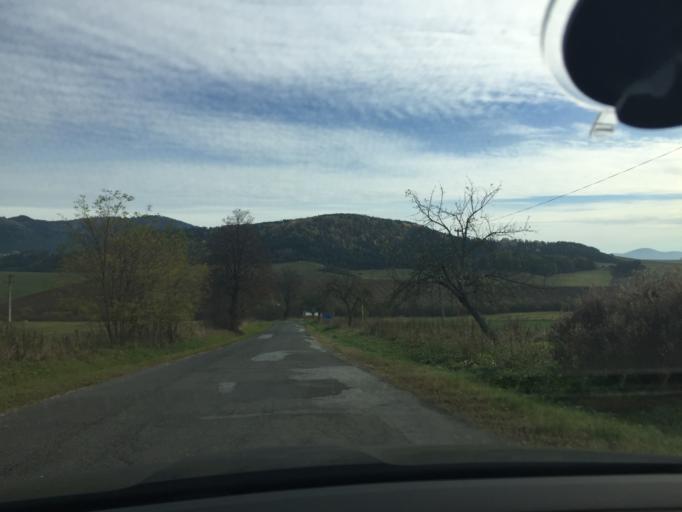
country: SK
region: Presovsky
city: Spisske Podhradie
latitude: 48.9881
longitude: 20.7911
